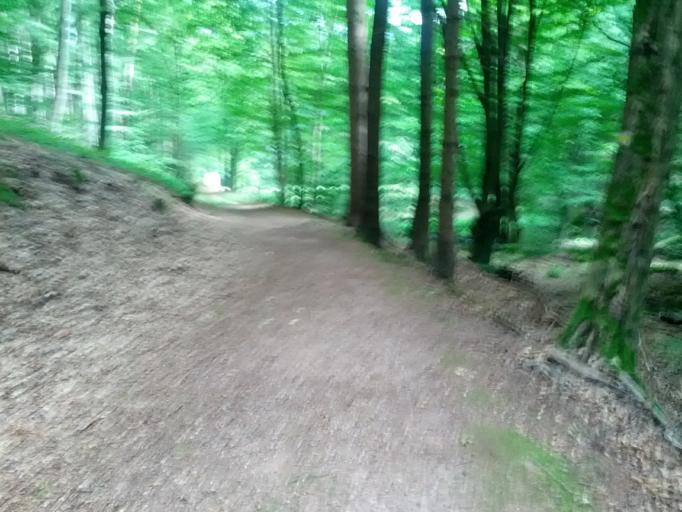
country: DE
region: Thuringia
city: Eisenach
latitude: 50.9475
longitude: 10.3025
